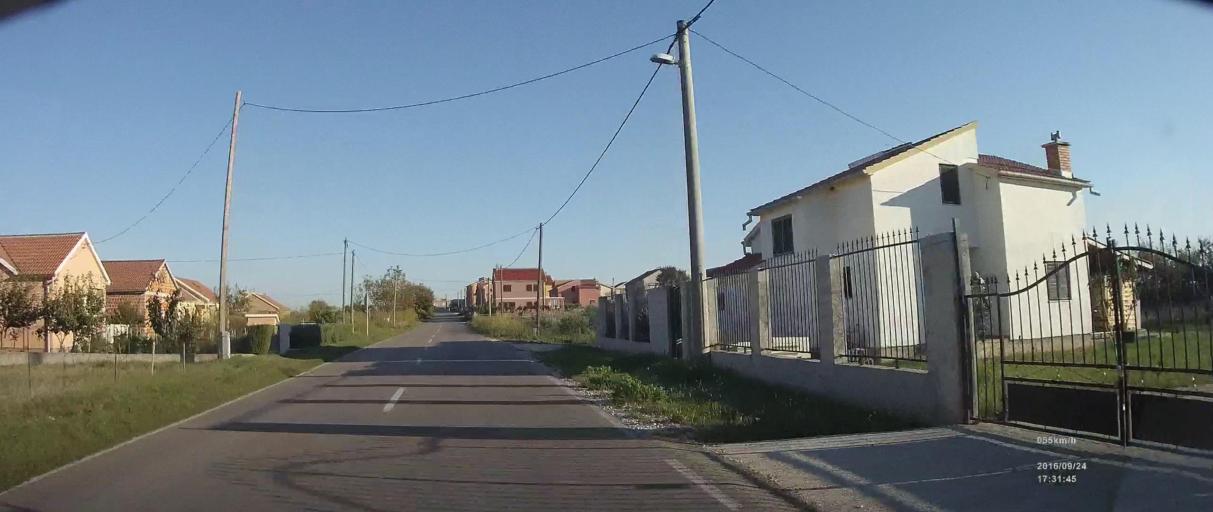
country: HR
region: Zadarska
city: Posedarje
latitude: 44.1869
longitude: 15.4449
